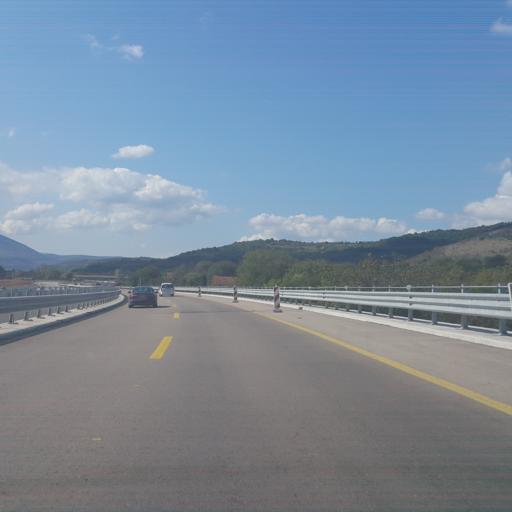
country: RS
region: Central Serbia
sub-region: Pirotski Okrug
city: Bela Palanka
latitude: 43.2349
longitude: 22.3739
